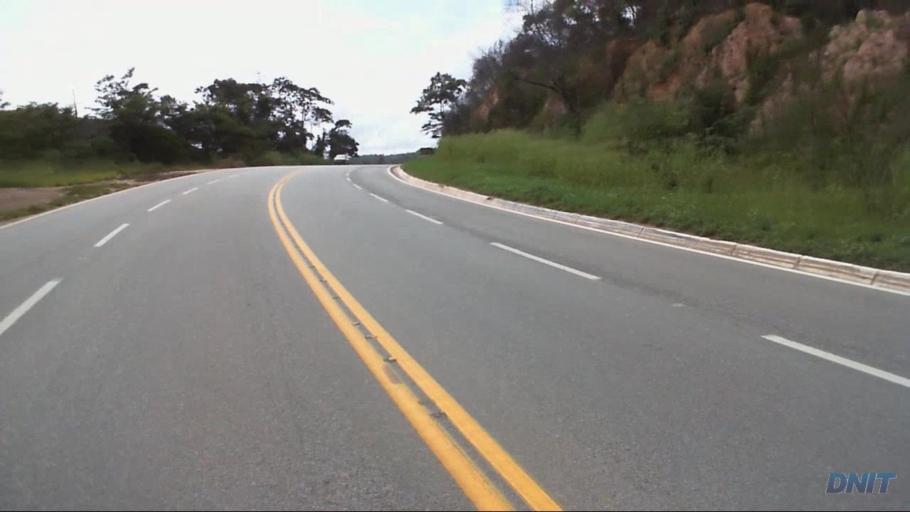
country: BR
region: Minas Gerais
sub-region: Caete
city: Caete
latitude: -19.7722
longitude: -43.6503
